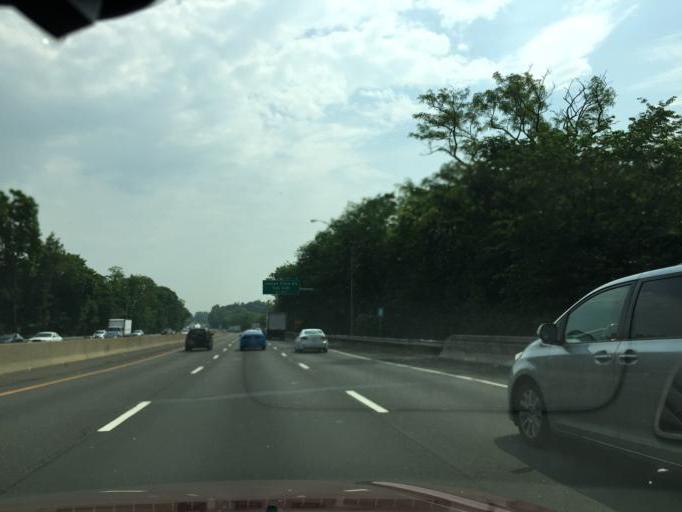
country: US
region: Connecticut
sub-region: Fairfield County
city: Greenwich
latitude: 41.0219
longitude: -73.6189
